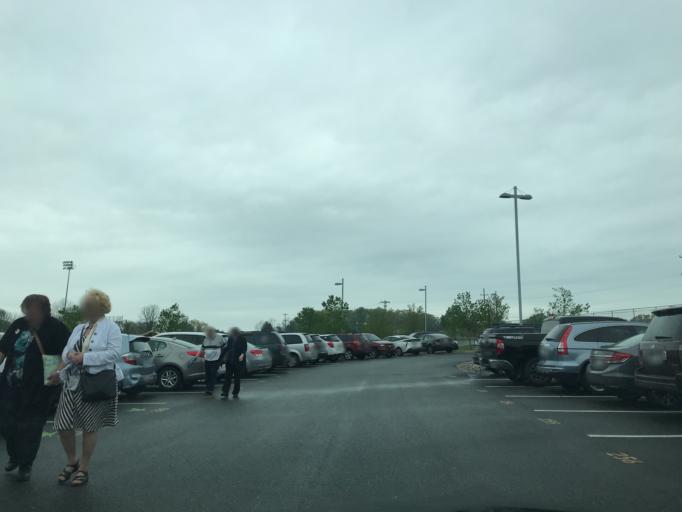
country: US
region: Pennsylvania
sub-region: York County
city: Susquehanna Trails
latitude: 39.6755
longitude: -76.4019
